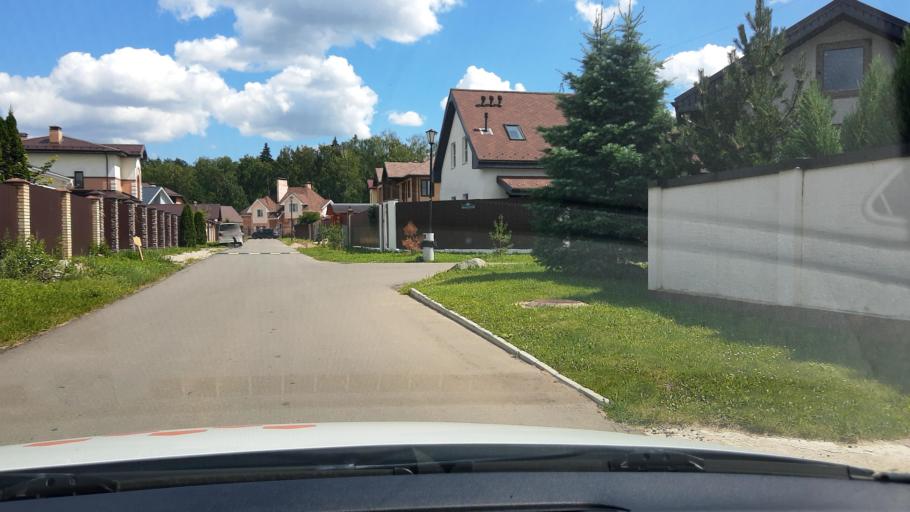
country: RU
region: Moskovskaya
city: Poselok Mar'ino
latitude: 55.5420
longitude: 37.3346
